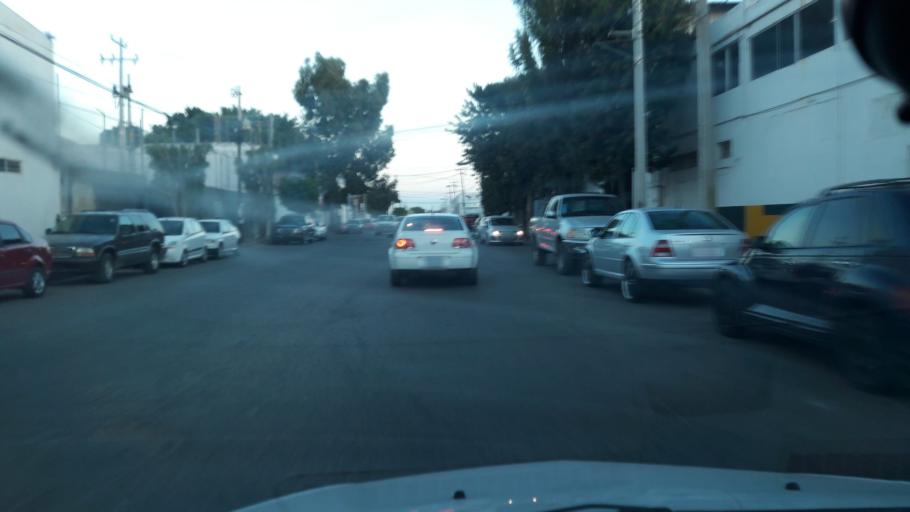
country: MX
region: Guanajuato
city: Leon
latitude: 21.1662
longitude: -101.6739
